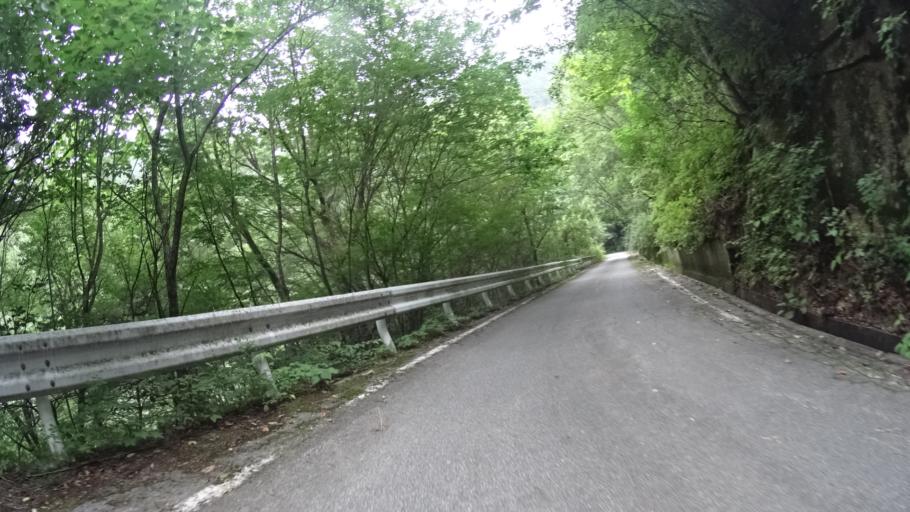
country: JP
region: Yamanashi
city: Kofu-shi
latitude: 35.8092
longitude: 138.6093
